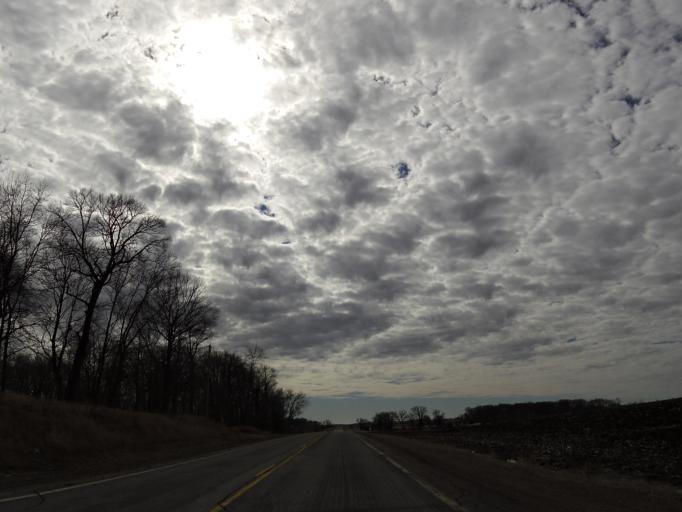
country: US
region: Minnesota
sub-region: Scott County
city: Prior Lake
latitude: 44.6928
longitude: -93.5211
